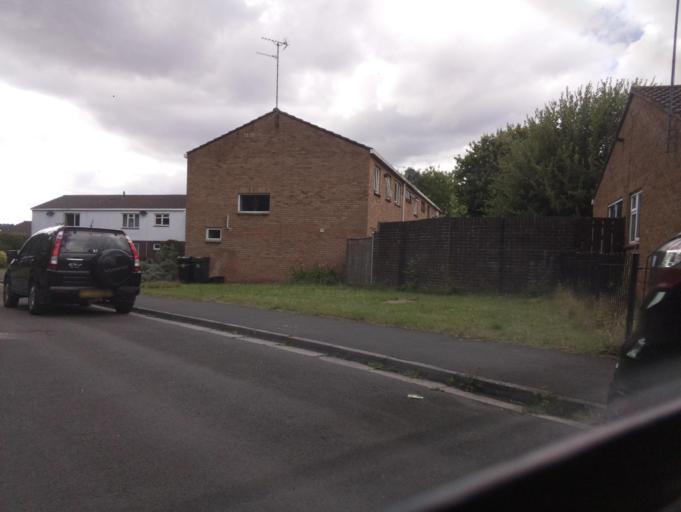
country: GB
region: England
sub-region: South Gloucestershire
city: Stoke Gifford
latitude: 51.4872
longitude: -2.5398
